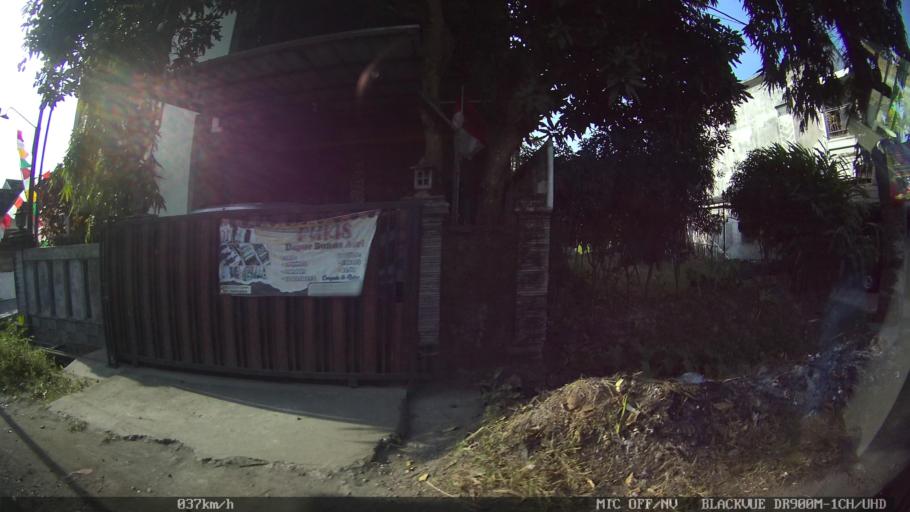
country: ID
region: Daerah Istimewa Yogyakarta
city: Sewon
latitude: -7.8670
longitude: 110.3400
